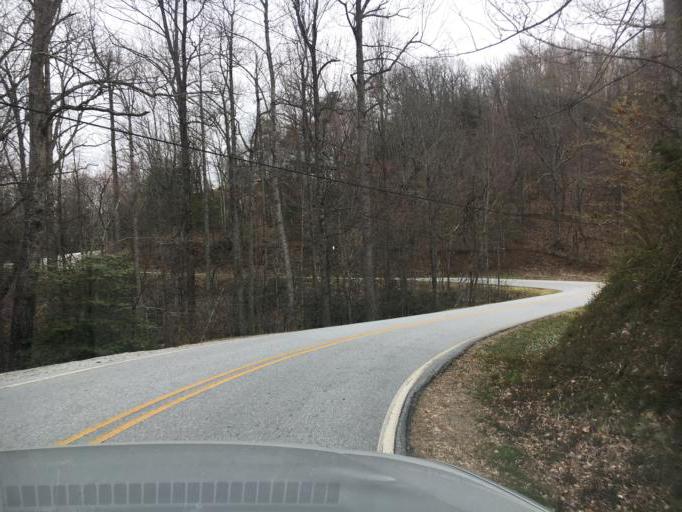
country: US
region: North Carolina
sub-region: Henderson County
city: East Flat Rock
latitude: 35.2544
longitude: -82.4156
